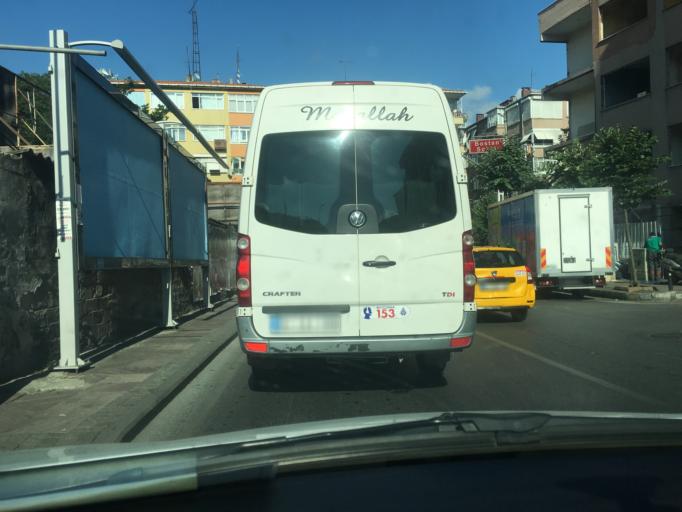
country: TR
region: Istanbul
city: Sisli
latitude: 41.0494
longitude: 29.0017
